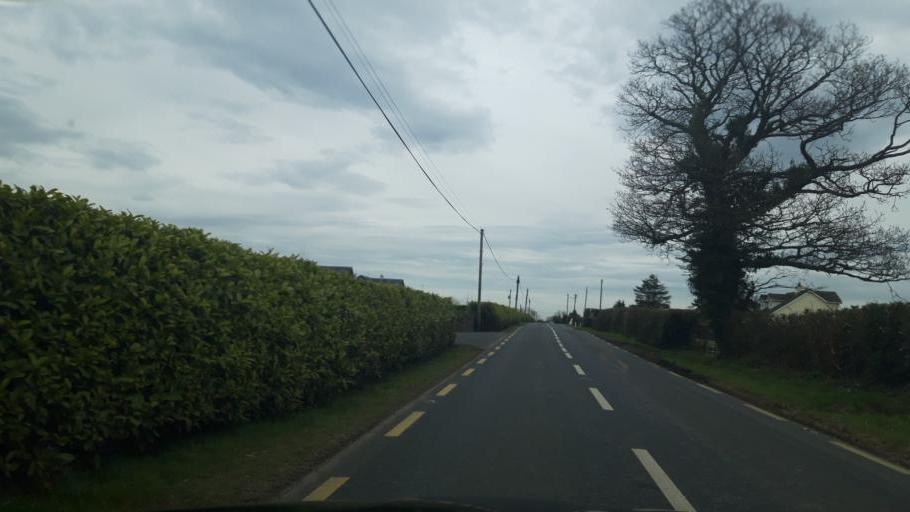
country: IE
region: Leinster
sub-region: Kildare
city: Clane
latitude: 53.3369
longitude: -6.6667
